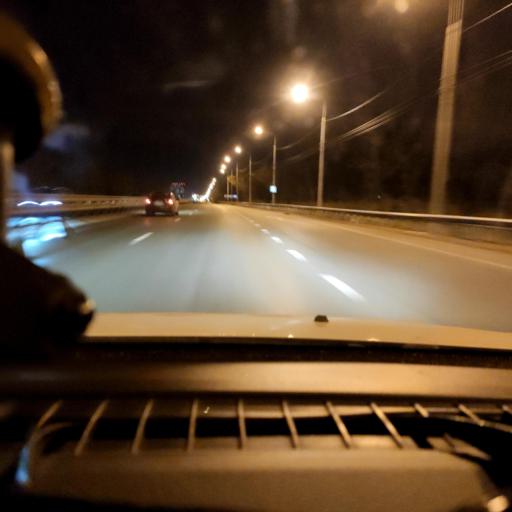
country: RU
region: Samara
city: Samara
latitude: 53.1027
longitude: 50.1621
